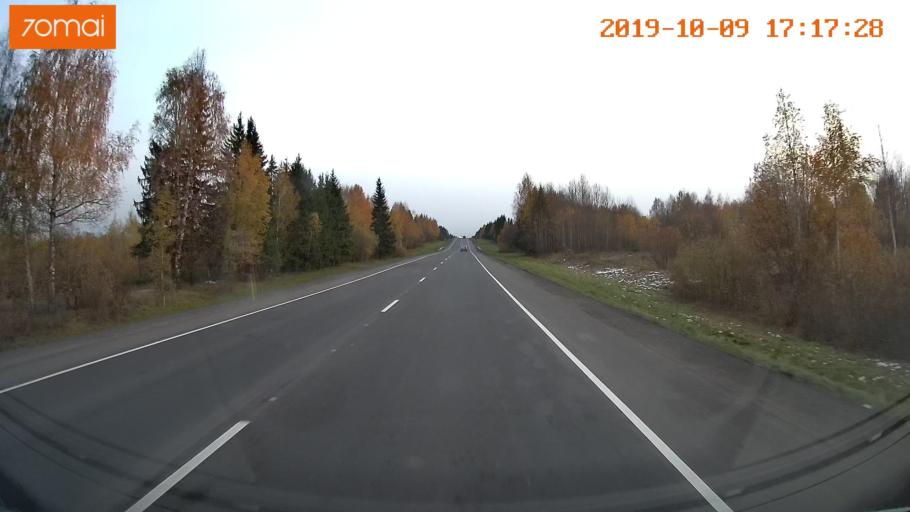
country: RU
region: Ivanovo
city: Furmanov
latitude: 57.2753
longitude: 41.1584
